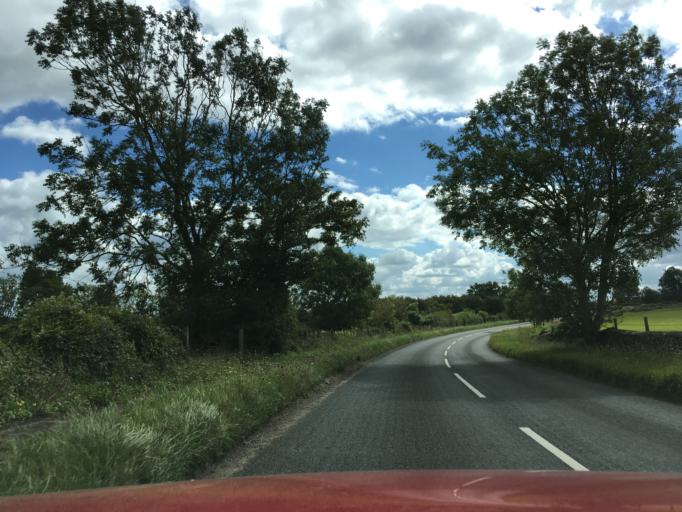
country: GB
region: England
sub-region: Wiltshire
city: Colerne
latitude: 51.4469
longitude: -2.2568
